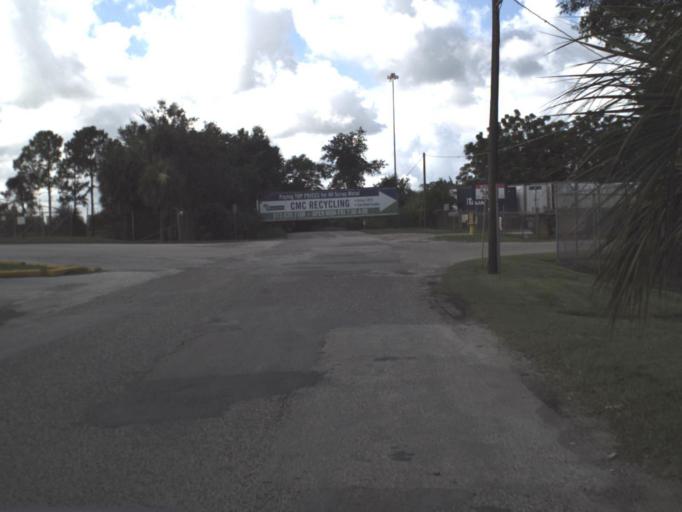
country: US
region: Florida
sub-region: Hillsborough County
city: East Lake-Orient Park
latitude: 27.9614
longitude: -82.3853
